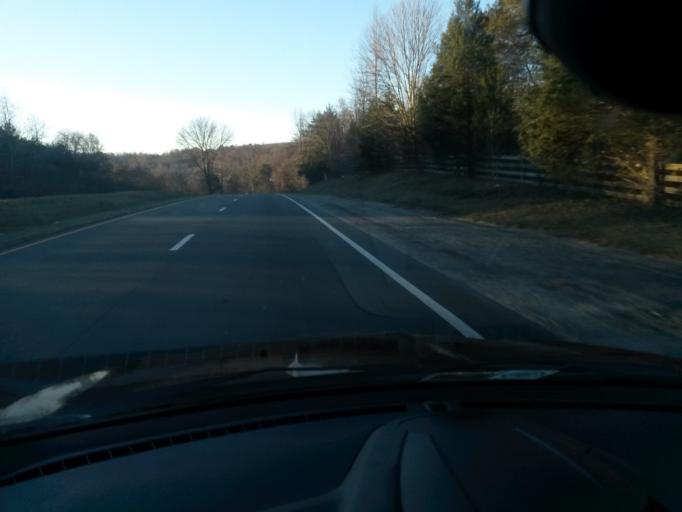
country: US
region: Virginia
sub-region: Franklin County
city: Henry Fork
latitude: 36.9352
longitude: -79.8740
